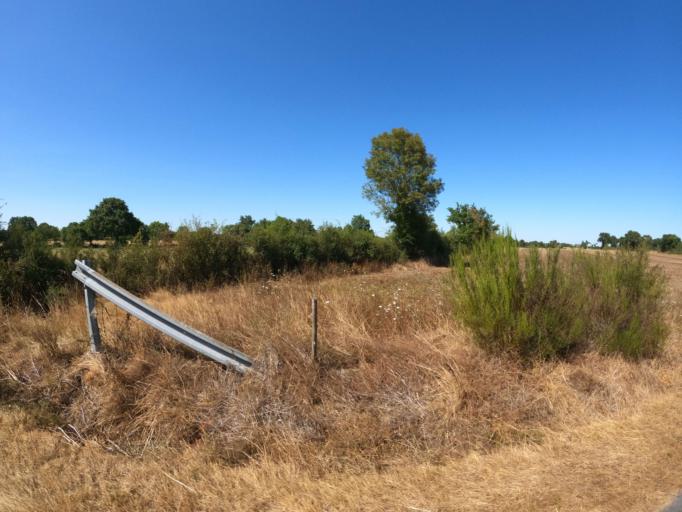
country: FR
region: Pays de la Loire
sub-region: Departement de la Vendee
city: La Boissiere-de-Montaigu
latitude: 46.9599
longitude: -1.1601
